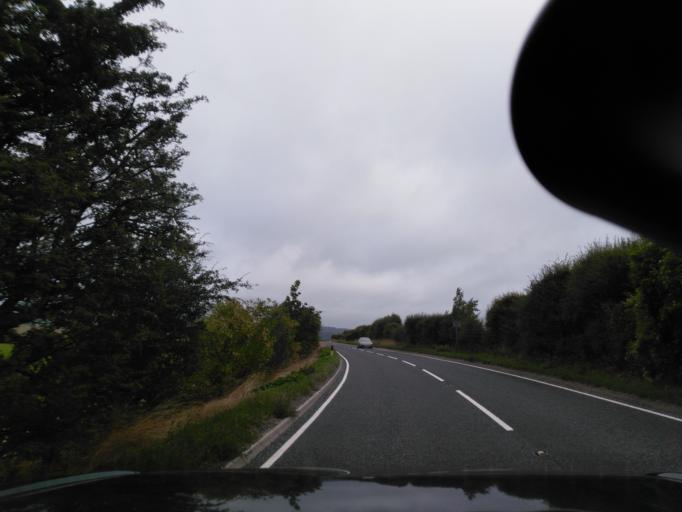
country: GB
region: England
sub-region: Wiltshire
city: Bishopstrow
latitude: 51.1471
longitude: -2.1612
